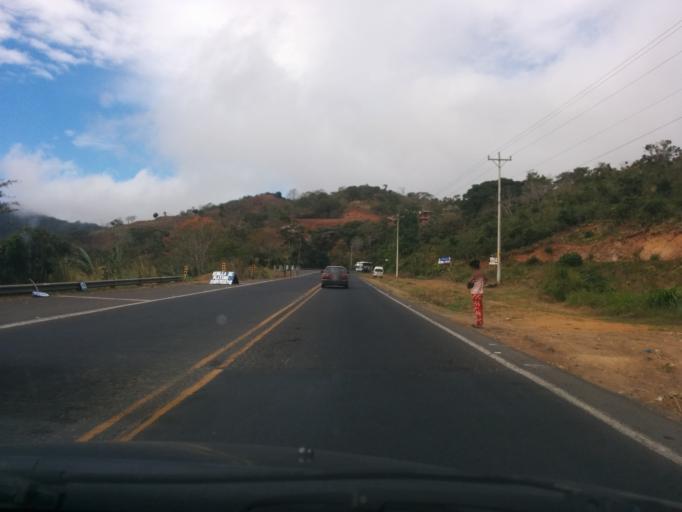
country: CR
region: Alajuela
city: San Rafael
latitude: 10.0619
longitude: -84.4495
